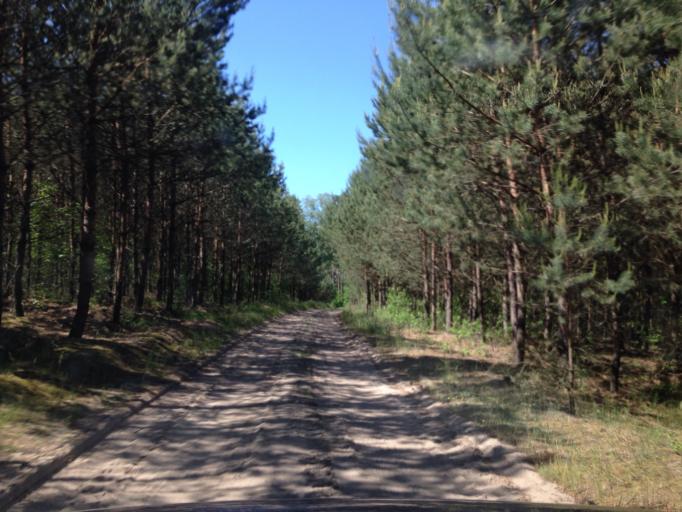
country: PL
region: Kujawsko-Pomorskie
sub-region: Powiat brodnicki
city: Bartniczka
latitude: 53.2651
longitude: 19.5541
